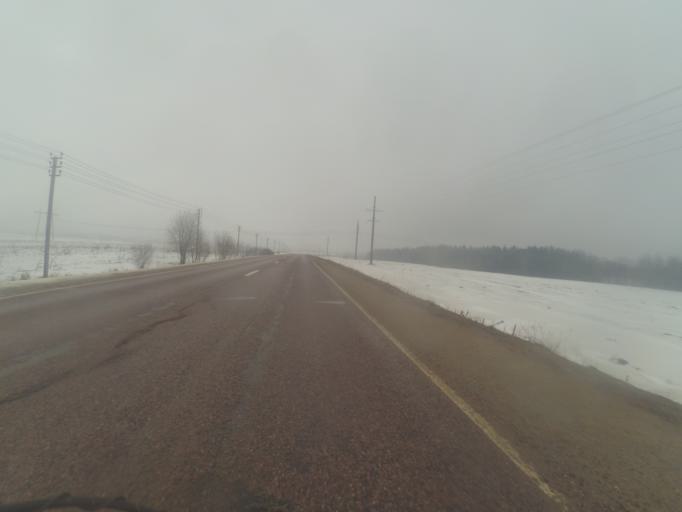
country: RU
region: Moskovskaya
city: Avtopoligon
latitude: 56.2621
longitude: 37.2308
